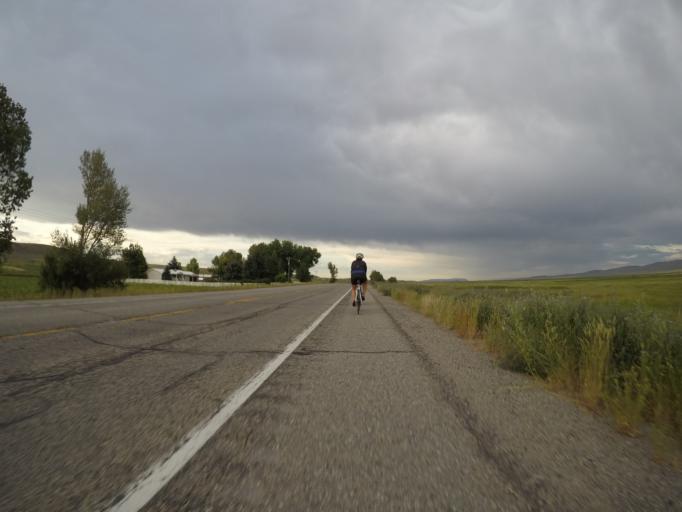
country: US
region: Utah
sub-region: Rich County
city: Randolph
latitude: 42.0263
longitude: -110.9327
